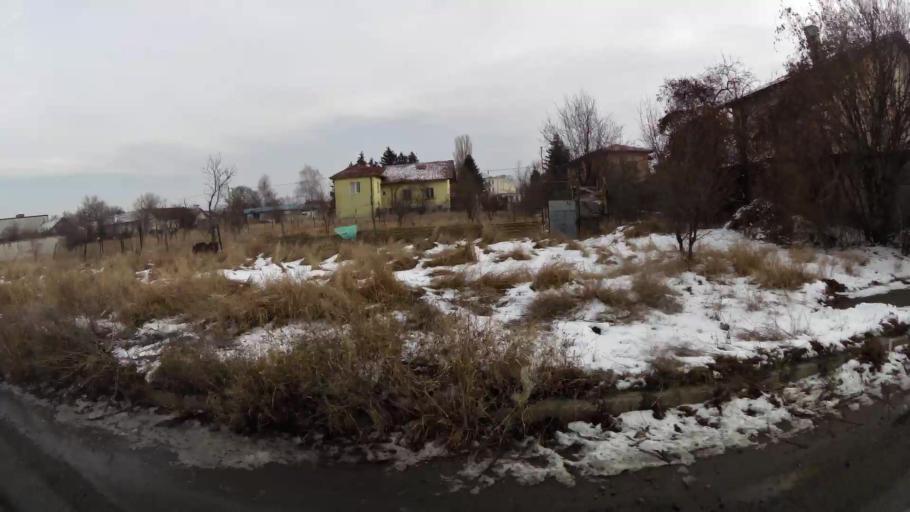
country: BG
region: Sofia-Capital
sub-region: Stolichna Obshtina
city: Sofia
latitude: 42.7111
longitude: 23.4120
